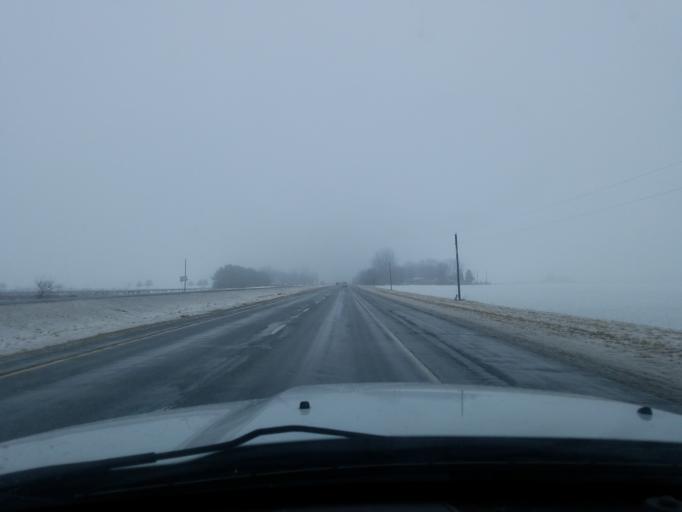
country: US
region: Indiana
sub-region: Tipton County
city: Tipton
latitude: 40.3041
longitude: -86.1268
